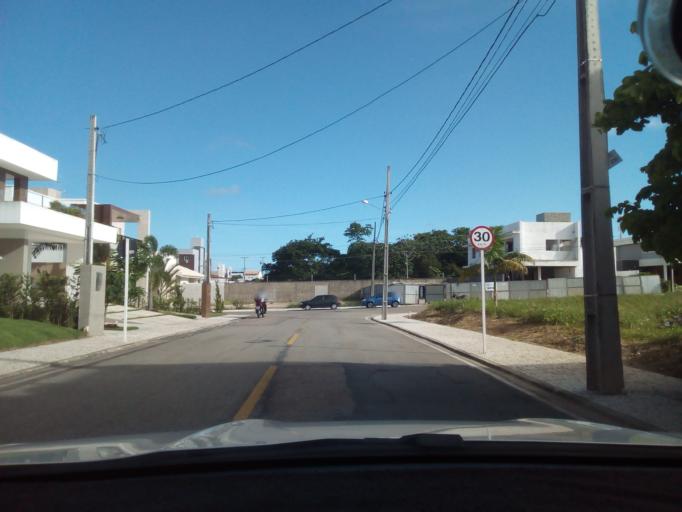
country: BR
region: Paraiba
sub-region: Joao Pessoa
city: Joao Pessoa
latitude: -7.1562
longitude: -34.8180
